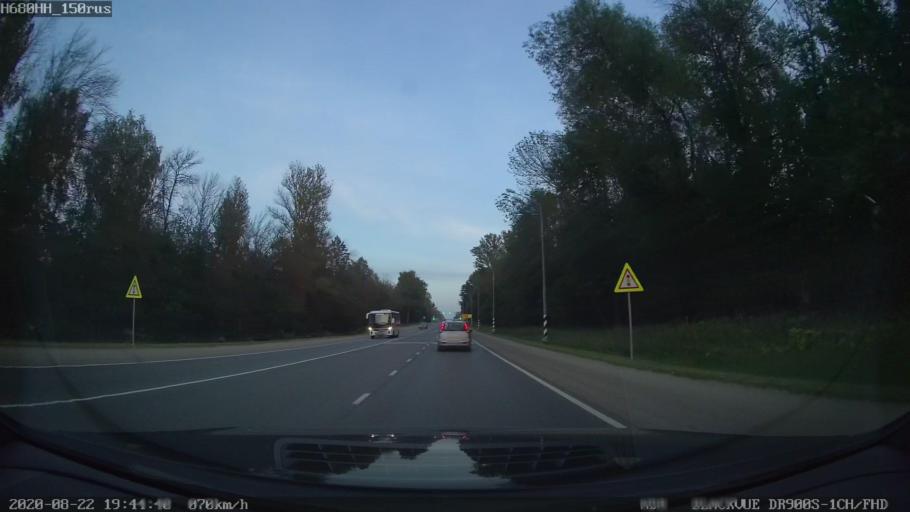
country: RU
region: Tverskaya
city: Emmaus
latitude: 56.7888
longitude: 36.0785
